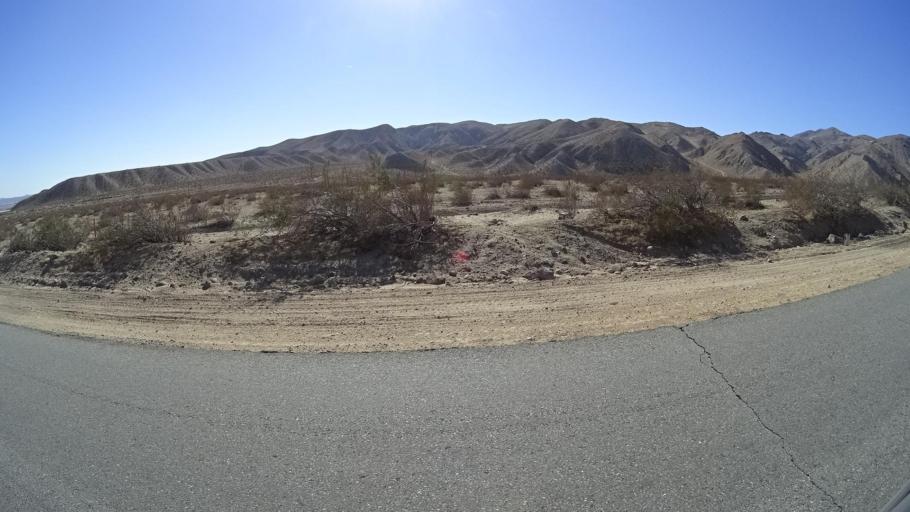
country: US
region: California
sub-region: Kern County
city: California City
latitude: 35.3118
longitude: -118.0253
